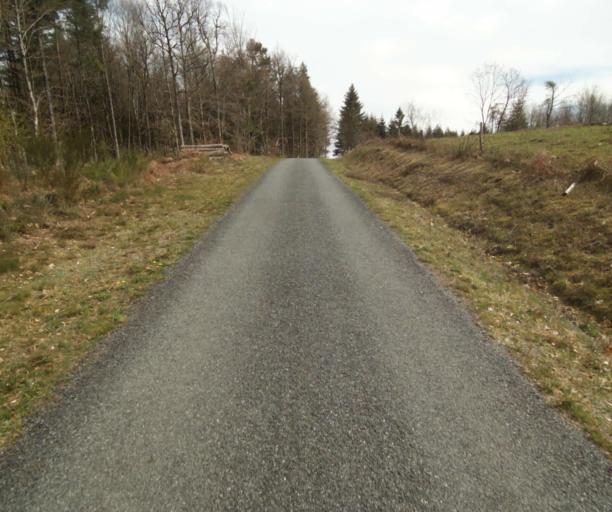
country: FR
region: Limousin
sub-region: Departement de la Correze
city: Correze
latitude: 45.3840
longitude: 1.9210
